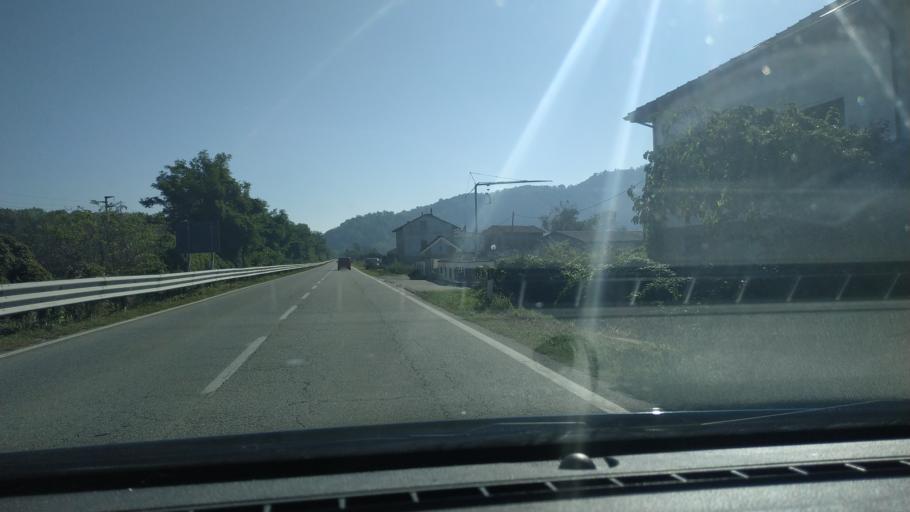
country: IT
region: Piedmont
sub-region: Provincia di Torino
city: San Sebastiano da Po
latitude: 45.1683
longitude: 7.9597
